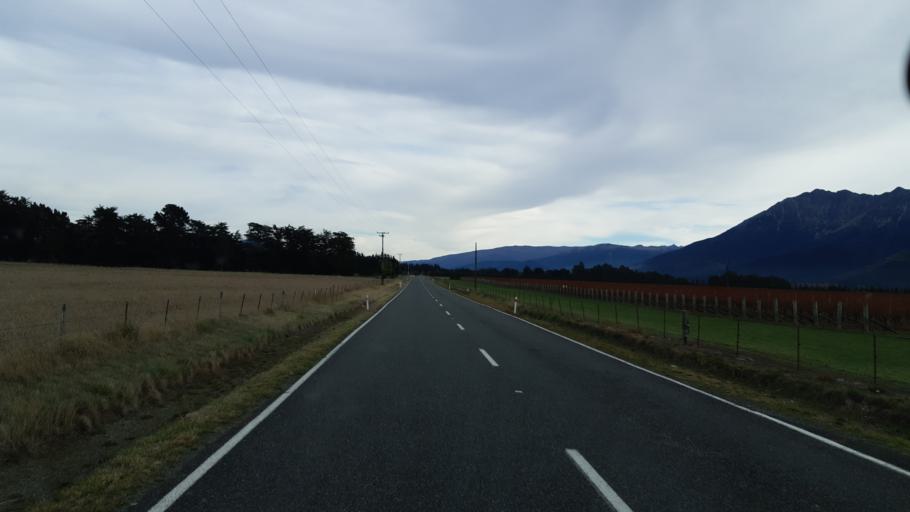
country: NZ
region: Tasman
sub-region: Tasman District
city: Brightwater
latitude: -41.6248
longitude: 173.3497
